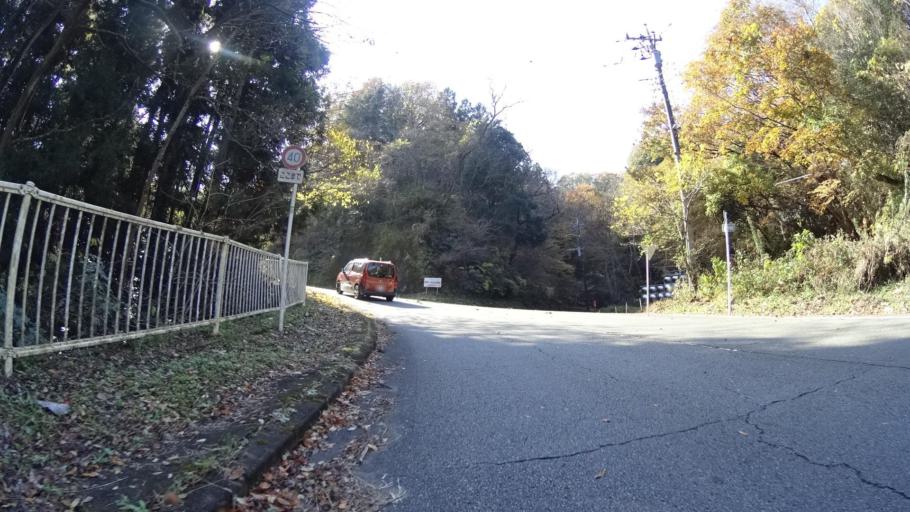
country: JP
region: Yamanashi
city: Uenohara
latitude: 35.5901
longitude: 139.1674
